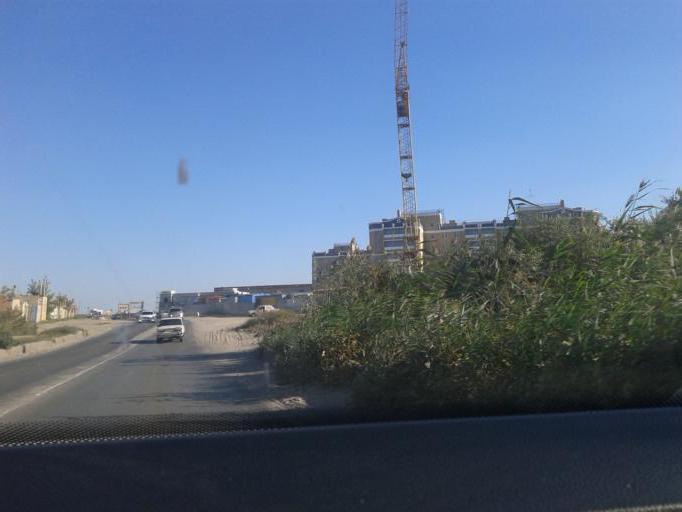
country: RU
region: Volgograd
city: Volgograd
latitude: 48.7675
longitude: 44.5097
